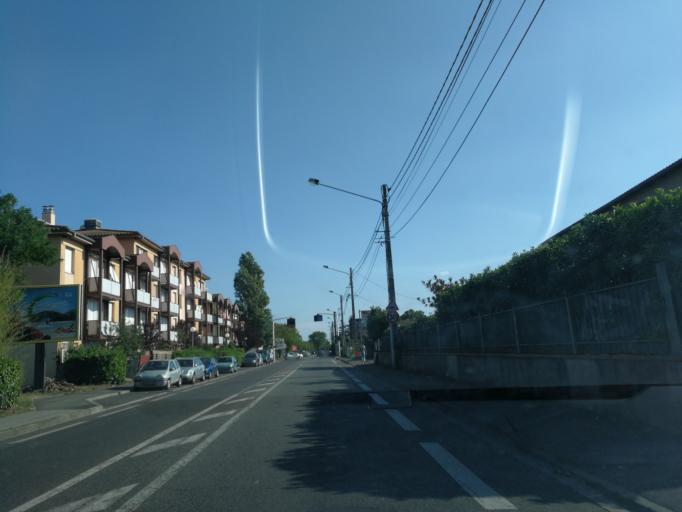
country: FR
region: Midi-Pyrenees
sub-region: Departement de la Haute-Garonne
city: Aucamville
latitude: 43.6418
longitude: 1.4391
